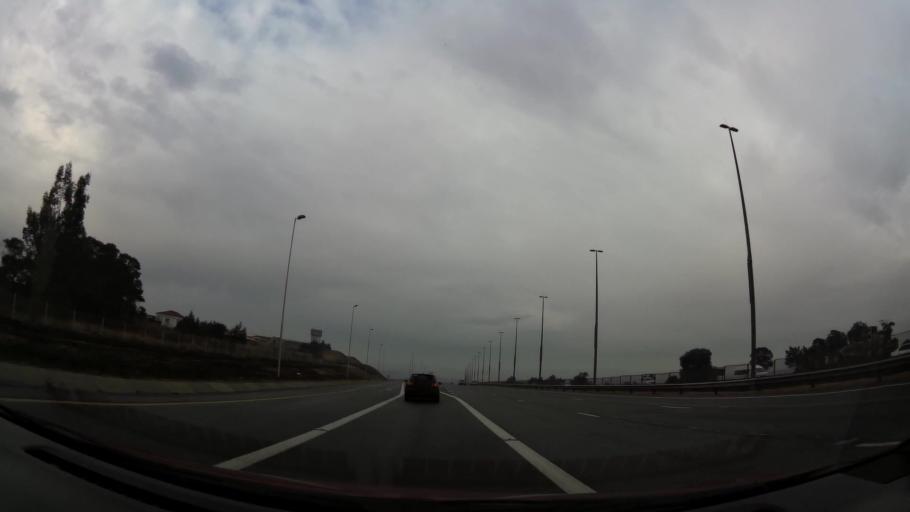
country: ZA
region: Gauteng
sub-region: City of Johannesburg Metropolitan Municipality
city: Soweto
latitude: -26.2961
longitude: 27.9464
